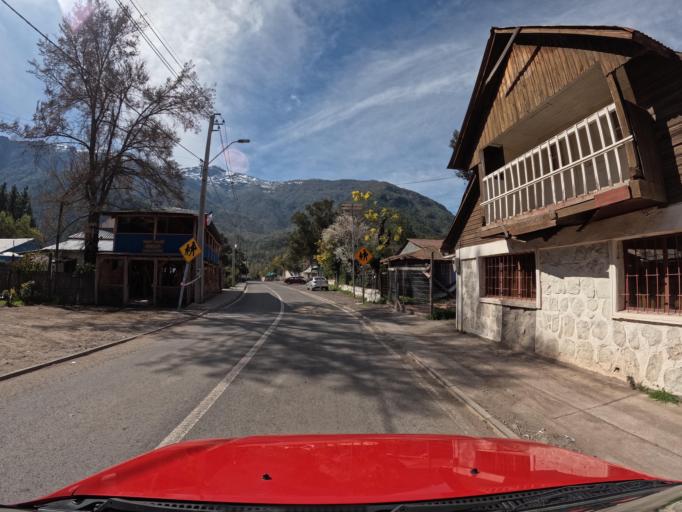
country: CL
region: O'Higgins
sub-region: Provincia de Colchagua
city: Chimbarongo
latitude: -35.0009
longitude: -70.8119
